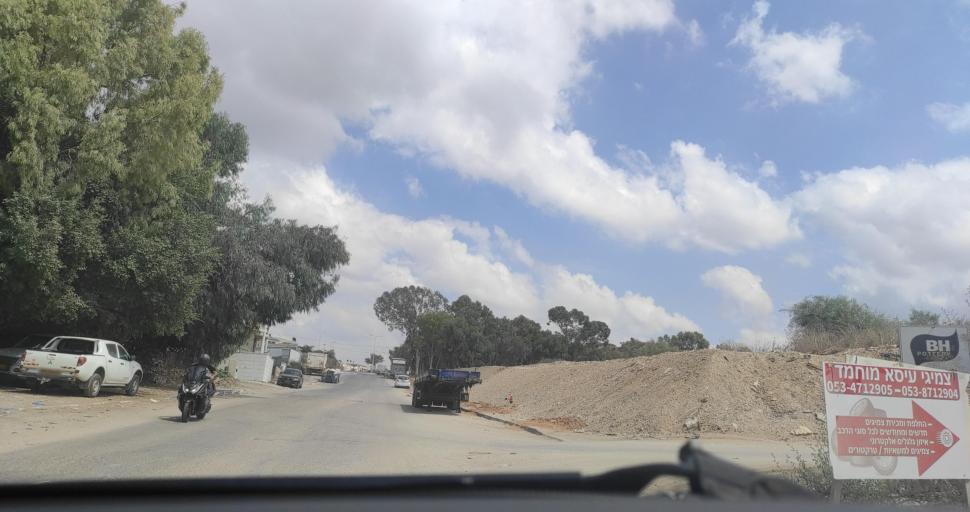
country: IL
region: Central District
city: Kafr Qasim
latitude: 32.1166
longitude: 34.9614
